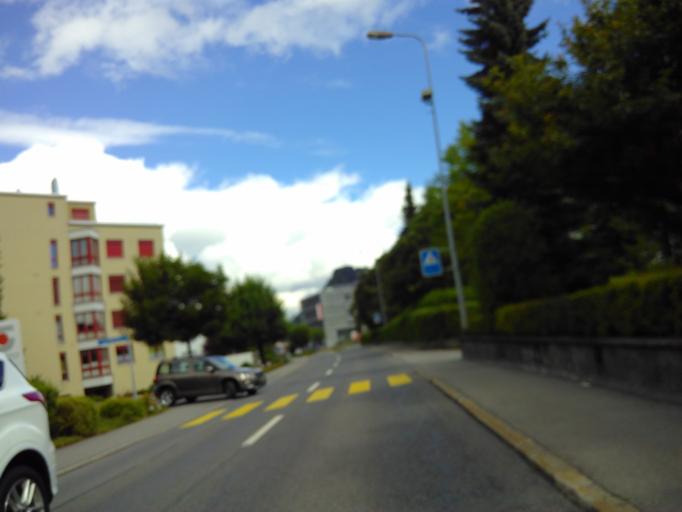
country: CH
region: Nidwalden
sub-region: Nidwalden
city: Stans
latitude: 46.9613
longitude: 8.3609
